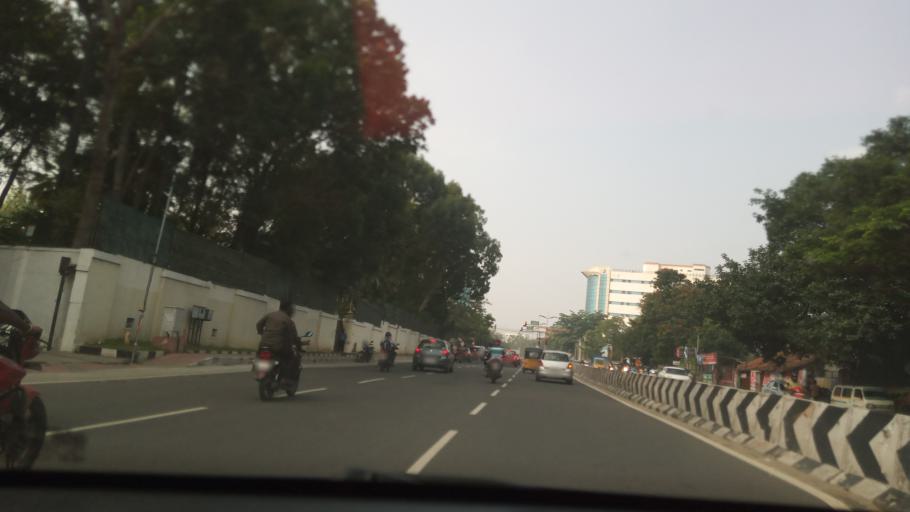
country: IN
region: Tamil Nadu
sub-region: Coimbatore
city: Coimbatore
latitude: 11.0111
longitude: 76.9833
